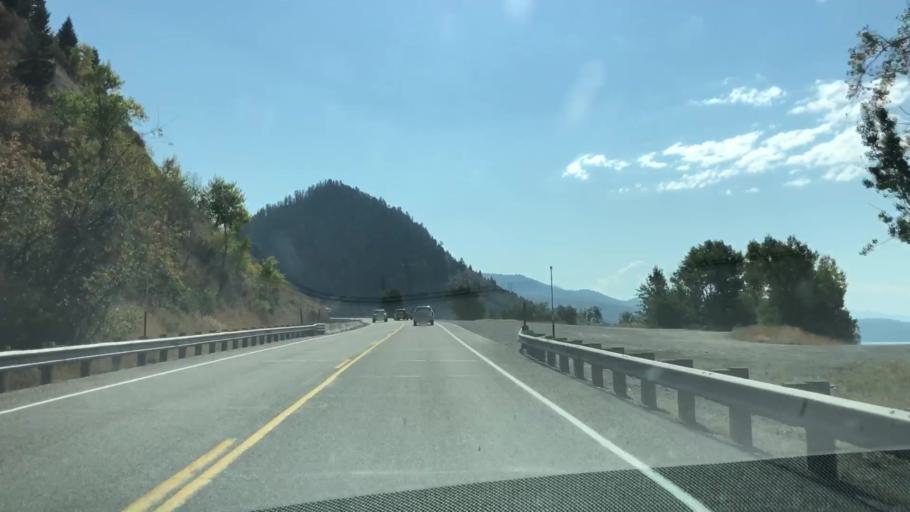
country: US
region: Idaho
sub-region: Teton County
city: Victor
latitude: 43.3197
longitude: -111.1561
